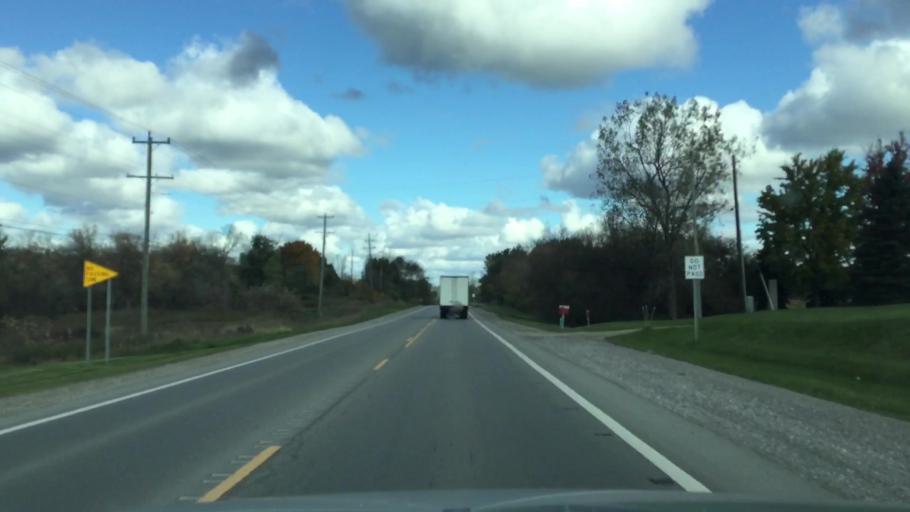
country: US
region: Michigan
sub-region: Oakland County
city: Oxford
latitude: 42.9067
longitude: -83.3121
